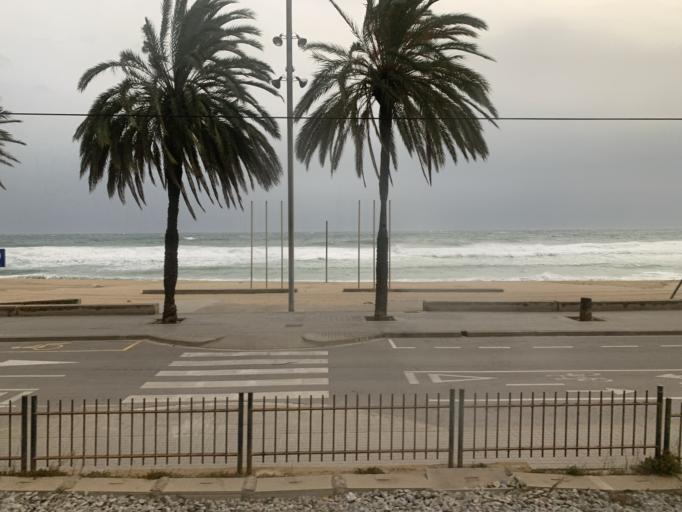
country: ES
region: Catalonia
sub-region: Provincia de Barcelona
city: Badalona
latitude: 41.4529
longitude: 2.2569
